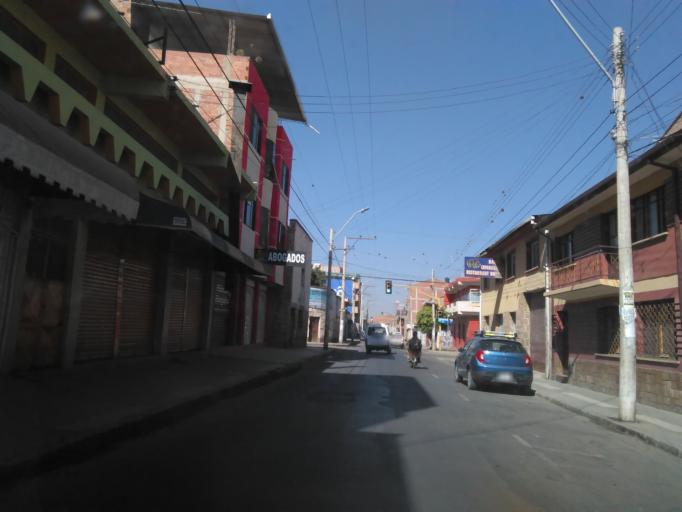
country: BO
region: Cochabamba
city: Sipe Sipe
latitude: -17.3997
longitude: -66.2796
